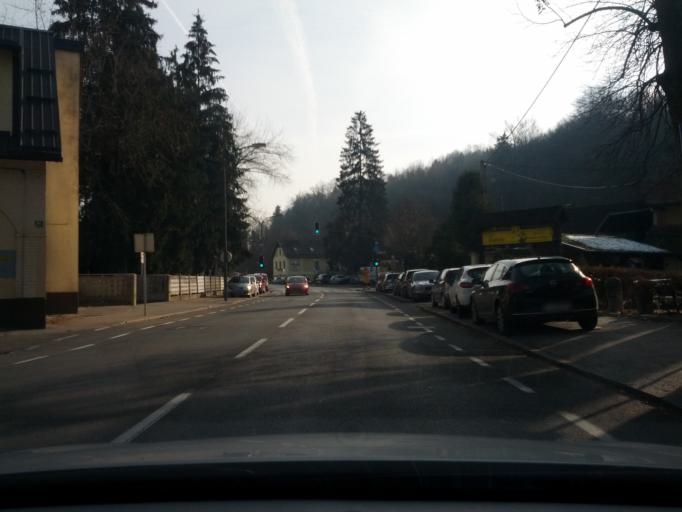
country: SI
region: Ljubljana
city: Ljubljana
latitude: 46.0675
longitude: 14.4859
